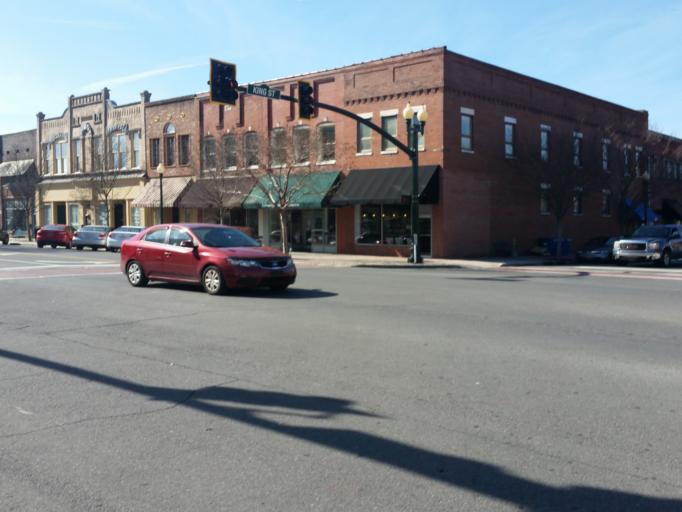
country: US
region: Georgia
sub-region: Whitfield County
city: Dalton
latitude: 34.7724
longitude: -84.9678
